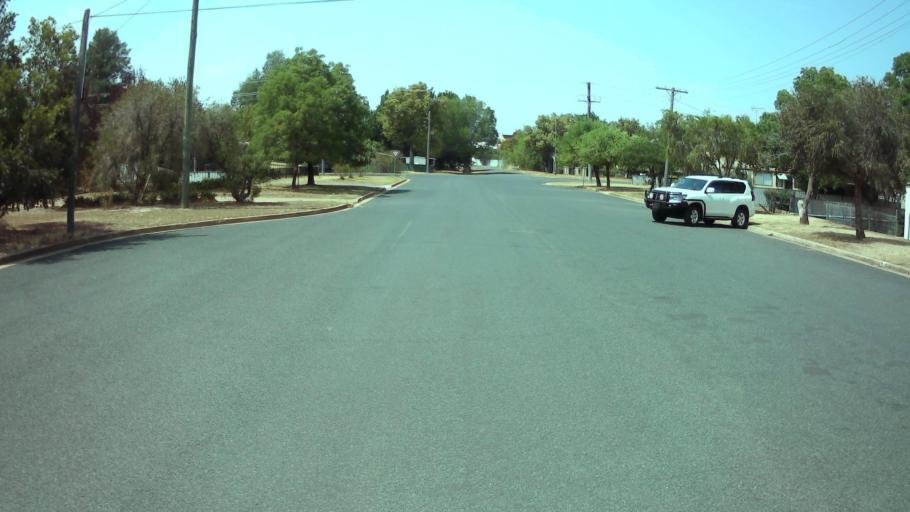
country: AU
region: New South Wales
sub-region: Weddin
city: Grenfell
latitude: -33.8913
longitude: 148.1587
